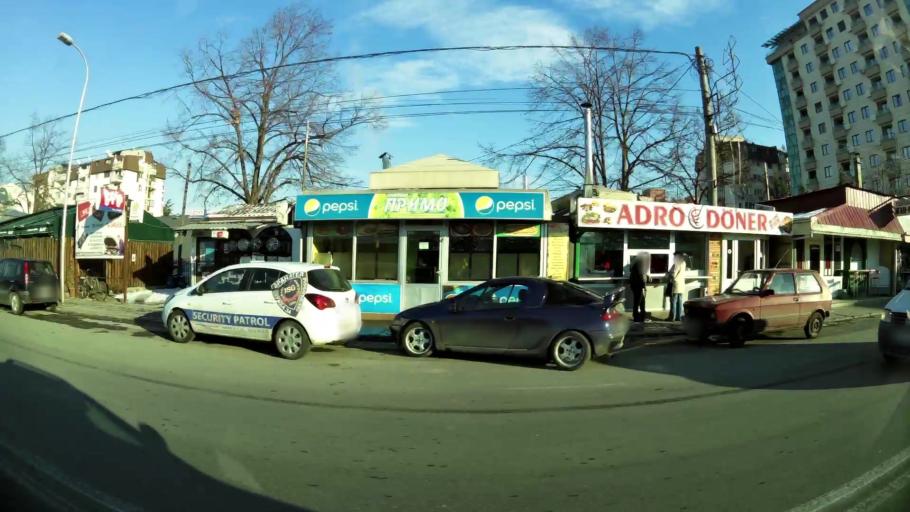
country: MK
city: Krushopek
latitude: 42.0010
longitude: 21.3896
